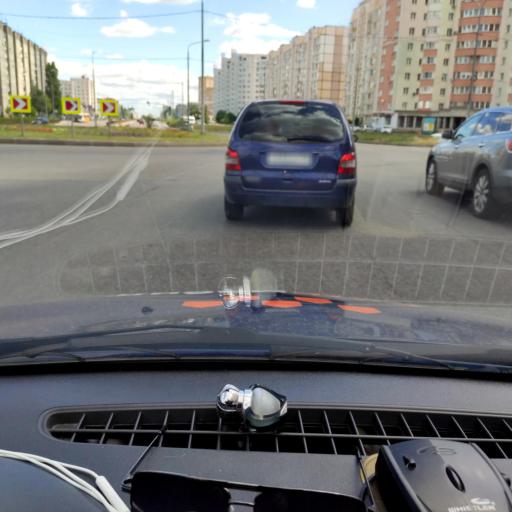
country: RU
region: Lipetsk
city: Syrskoye
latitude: 52.5813
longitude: 39.5137
